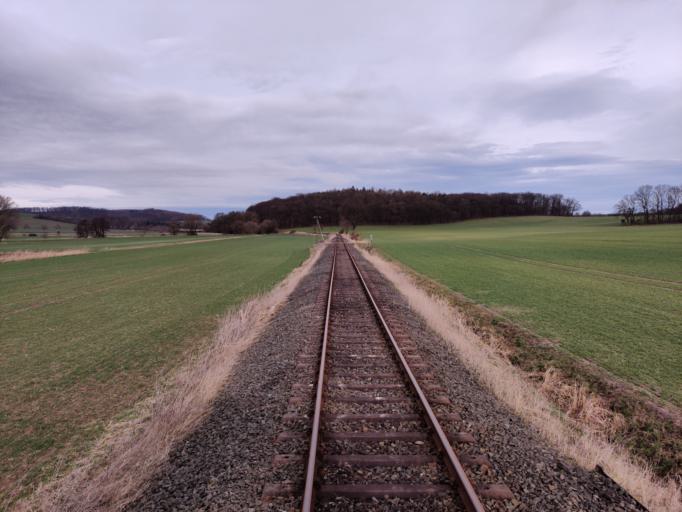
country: DE
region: Lower Saxony
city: Haverlah
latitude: 52.0576
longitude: 10.1378
